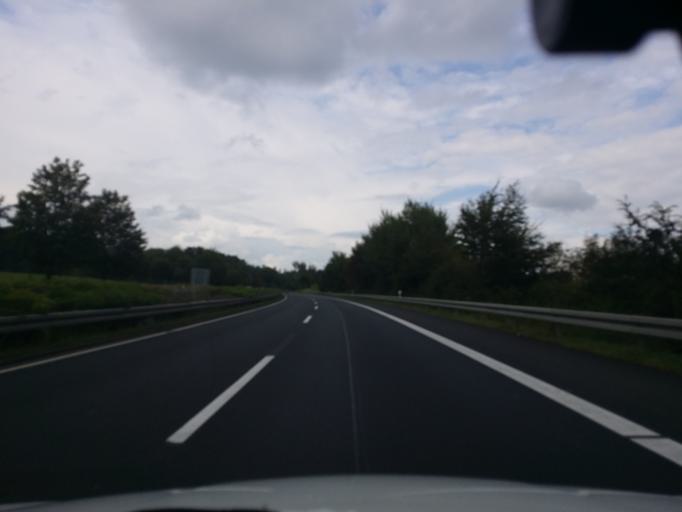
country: DE
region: Hesse
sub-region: Regierungsbezirk Darmstadt
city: Steinau an der Strasse
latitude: 50.3342
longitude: 9.4850
